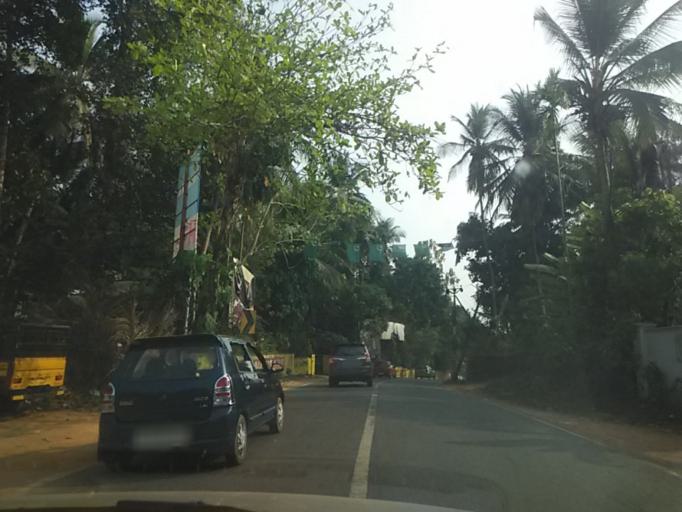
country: IN
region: Kerala
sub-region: Kozhikode
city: Naduvannur
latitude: 11.4739
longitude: 75.7744
